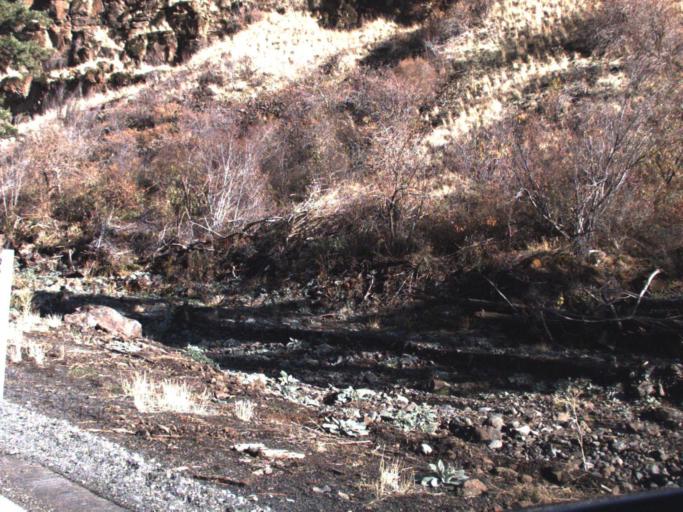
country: US
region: Washington
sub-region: Asotin County
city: Asotin
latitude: 46.0464
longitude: -117.2430
